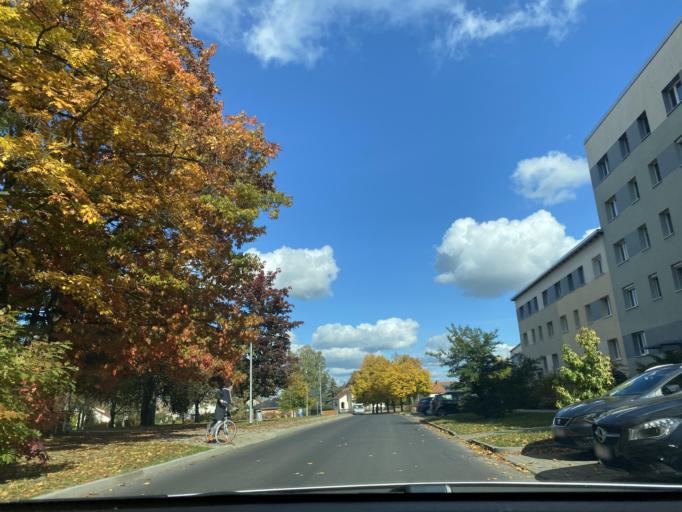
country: DE
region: Saxony
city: Weisswasser
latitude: 51.5011
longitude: 14.6270
